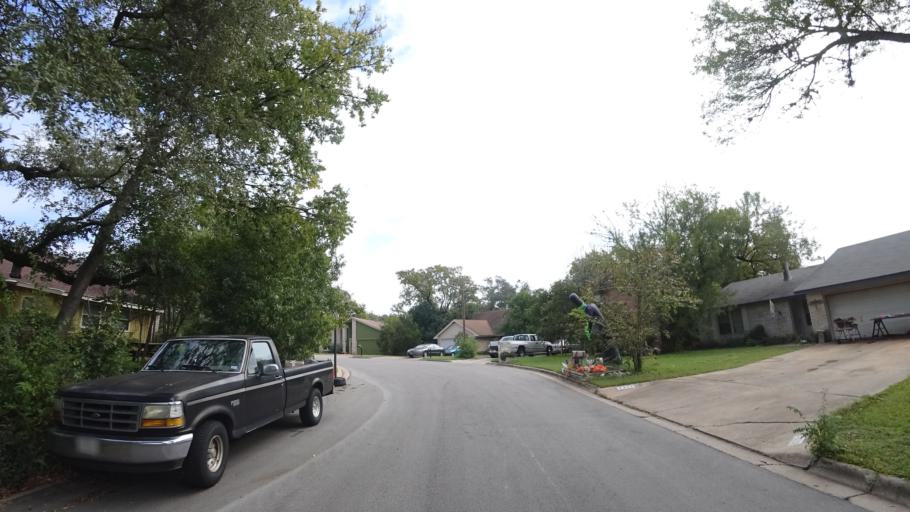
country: US
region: Texas
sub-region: Travis County
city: Shady Hollow
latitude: 30.1980
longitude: -97.8319
